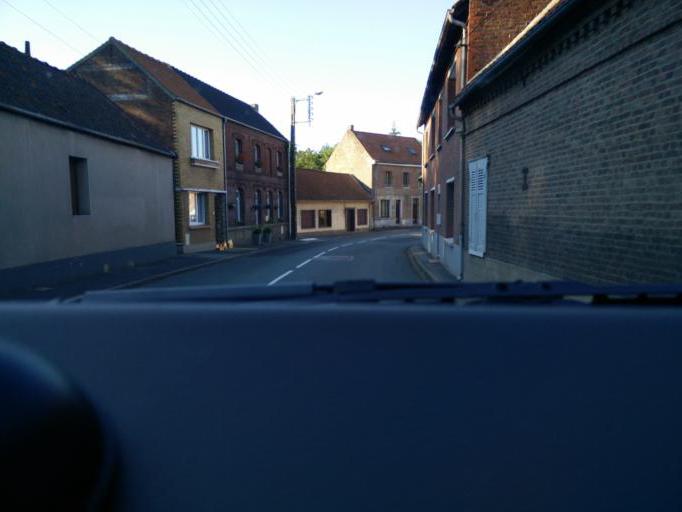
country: FR
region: Nord-Pas-de-Calais
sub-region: Departement du Pas-de-Calais
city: Divion
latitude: 50.4566
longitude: 2.4819
